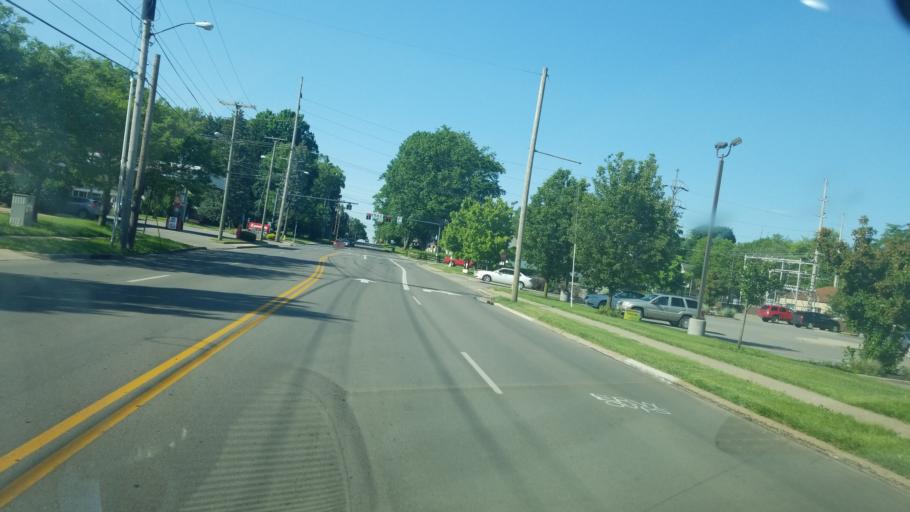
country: US
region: Ohio
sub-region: Wayne County
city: Wooster
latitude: 40.8236
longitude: -81.9340
